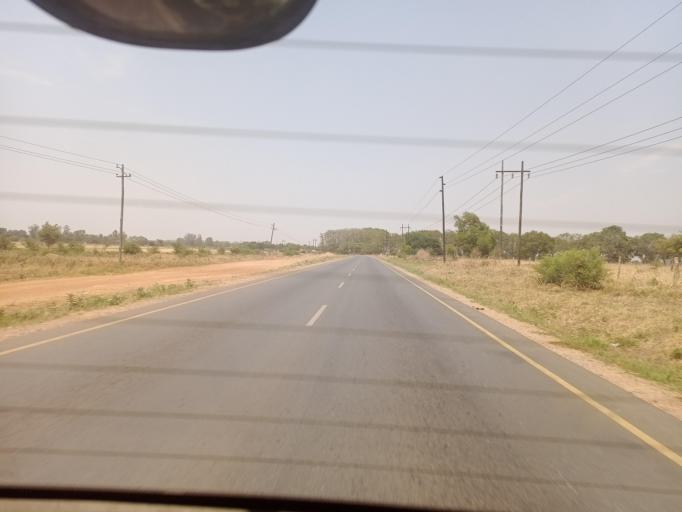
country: ZM
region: Lusaka
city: Lusaka
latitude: -15.2717
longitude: 28.4094
